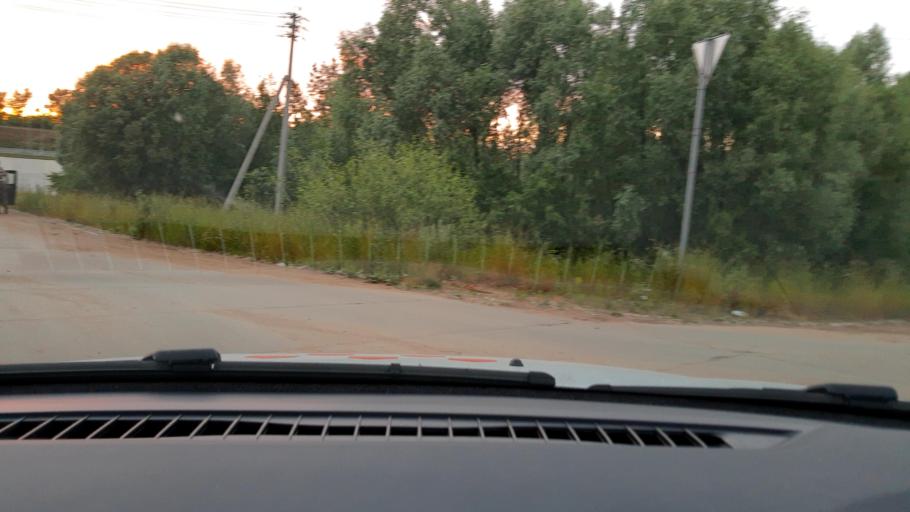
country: RU
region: Nizjnij Novgorod
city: Neklyudovo
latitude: 56.3646
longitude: 43.9392
